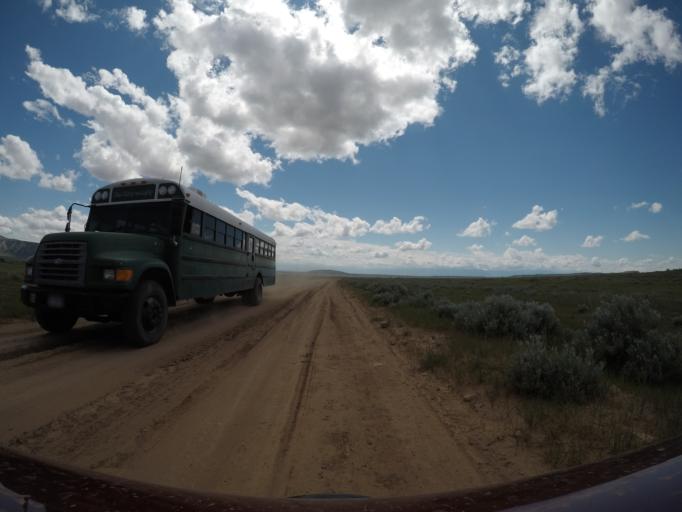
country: US
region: Montana
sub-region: Yellowstone County
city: Laurel
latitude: 45.2380
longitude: -108.6768
